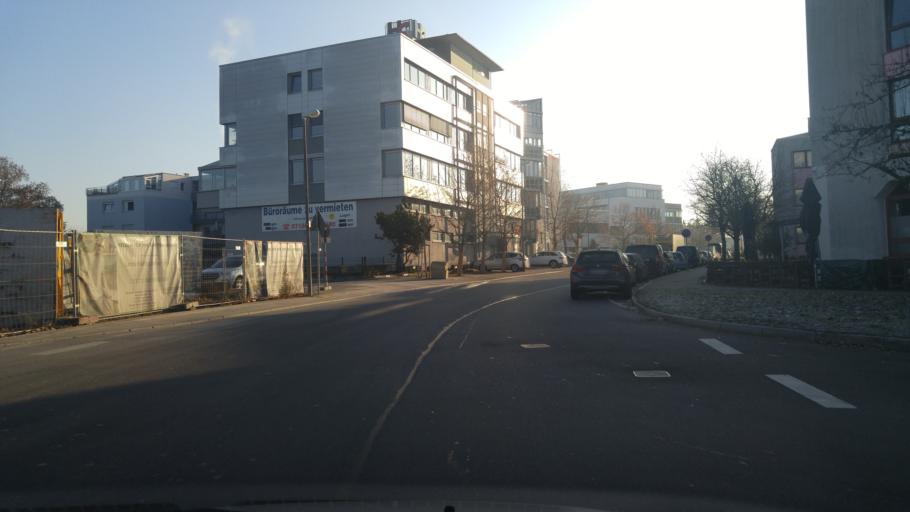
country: DE
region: Baden-Wuerttemberg
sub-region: Regierungsbezirk Stuttgart
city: Gerlingen
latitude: 48.8070
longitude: 9.0708
